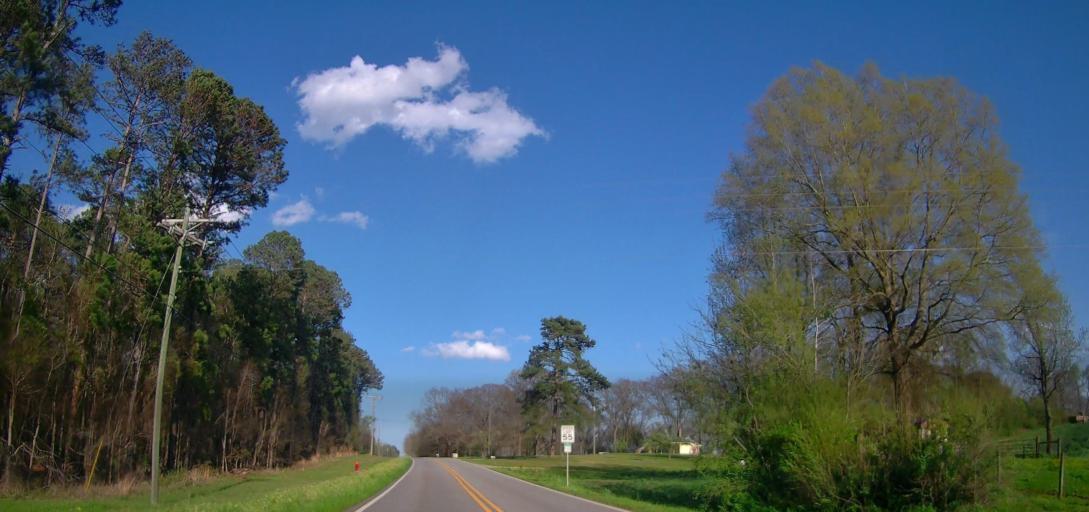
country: US
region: Georgia
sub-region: Putnam County
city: Eatonton
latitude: 33.1967
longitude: -83.4170
